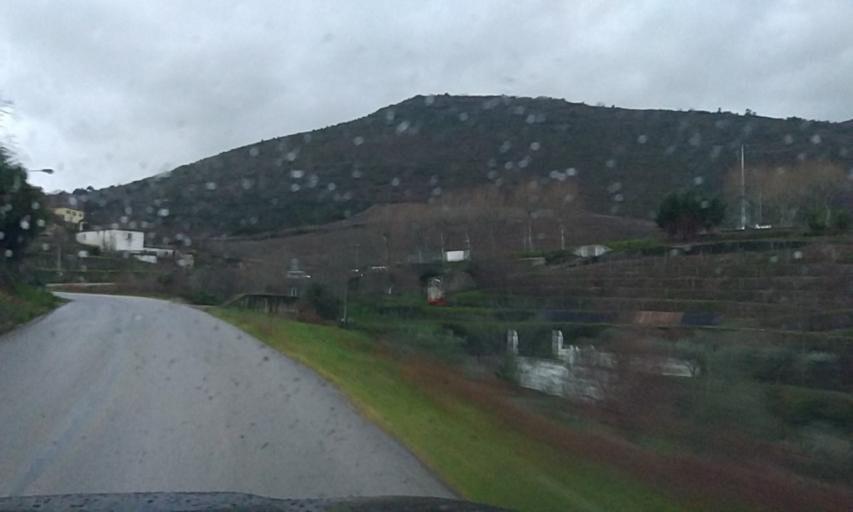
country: PT
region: Vila Real
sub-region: Sabrosa
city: Vilela
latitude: 41.2279
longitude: -7.5623
